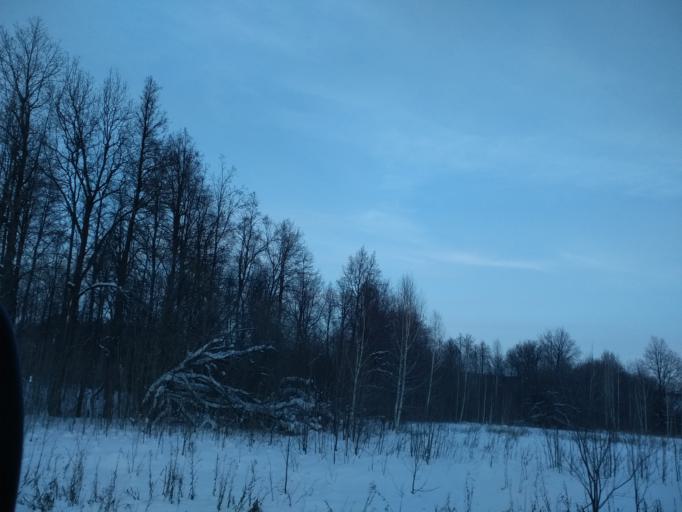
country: RU
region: Bashkortostan
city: Kudeyevskiy
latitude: 54.7213
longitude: 56.6086
